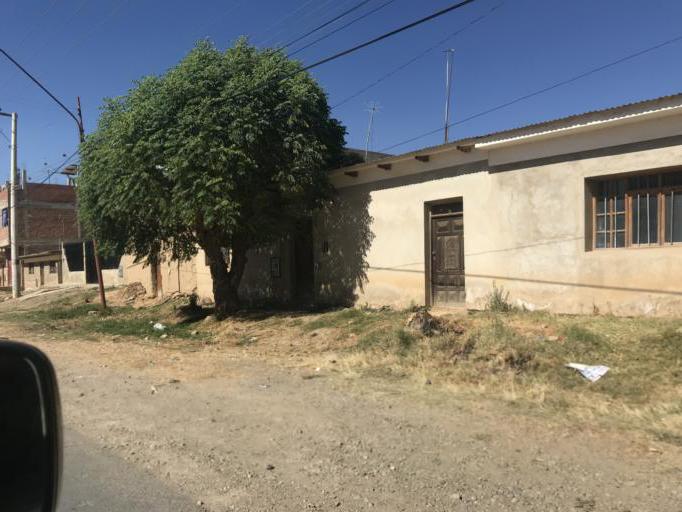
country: BO
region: Cochabamba
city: Cliza
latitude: -17.5795
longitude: -65.9100
